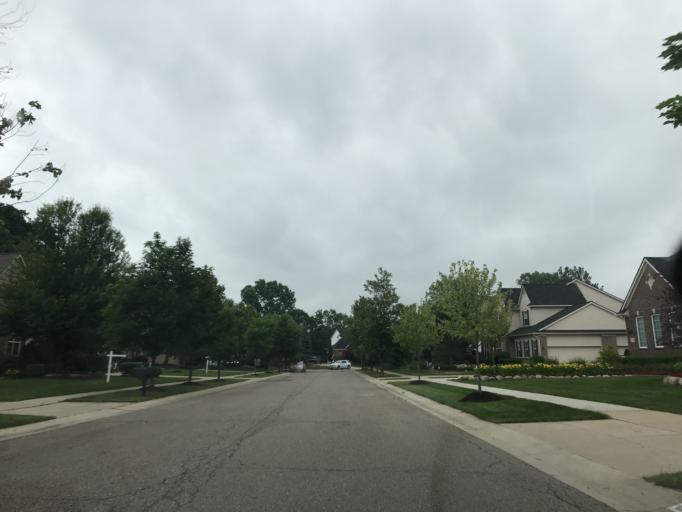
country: US
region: Michigan
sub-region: Oakland County
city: South Lyon
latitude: 42.4821
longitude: -83.6450
